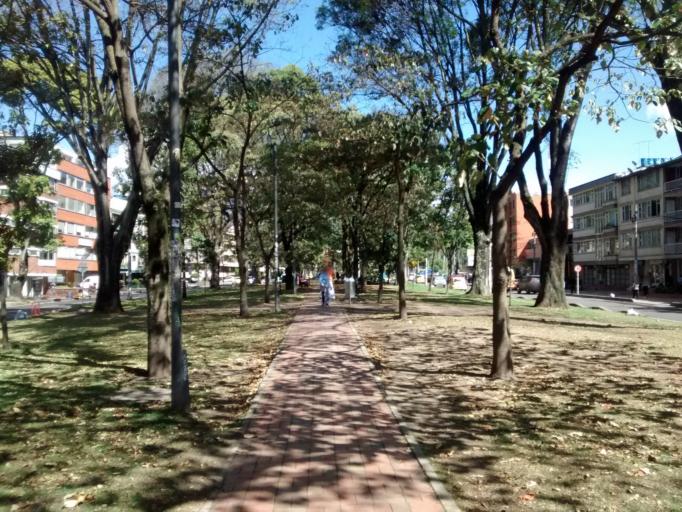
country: CO
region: Bogota D.C.
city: Bogota
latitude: 4.6336
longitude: -74.0753
